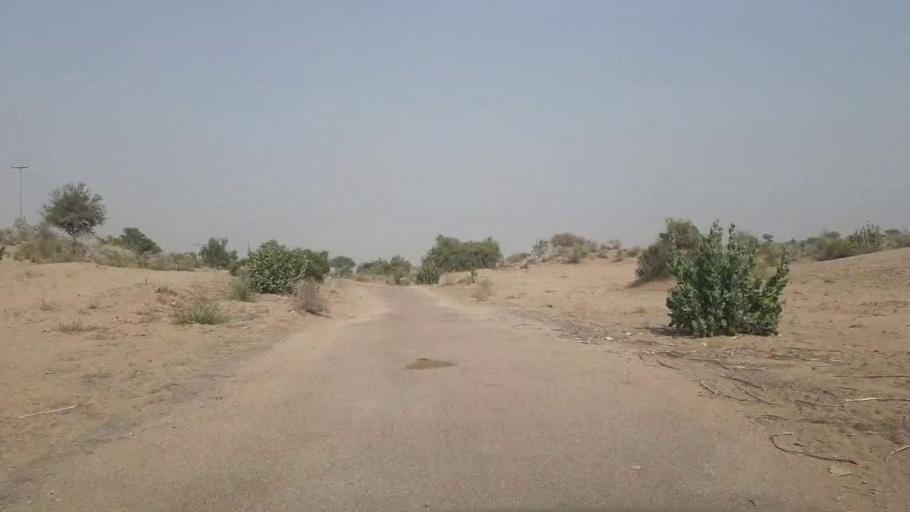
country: PK
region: Sindh
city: Chor
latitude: 25.6276
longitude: 70.0320
